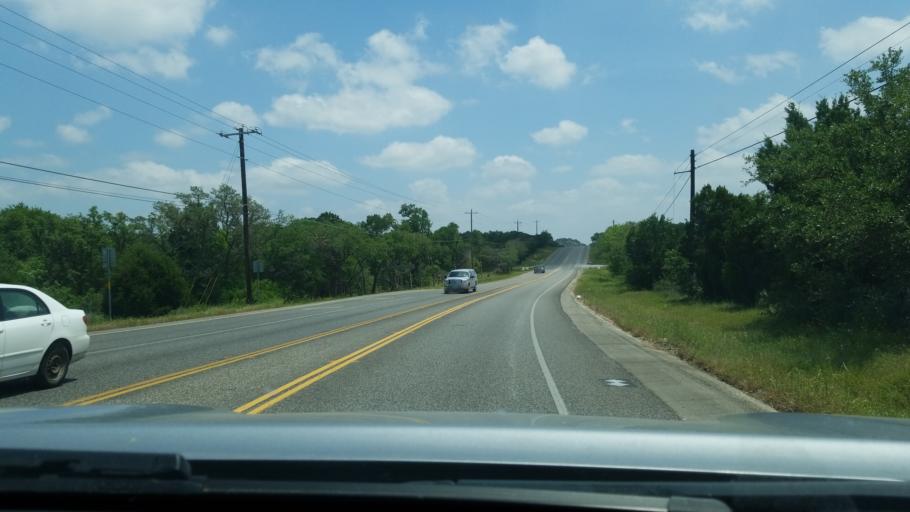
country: US
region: Texas
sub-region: Hays County
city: Woodcreek
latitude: 30.0191
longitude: -98.1301
